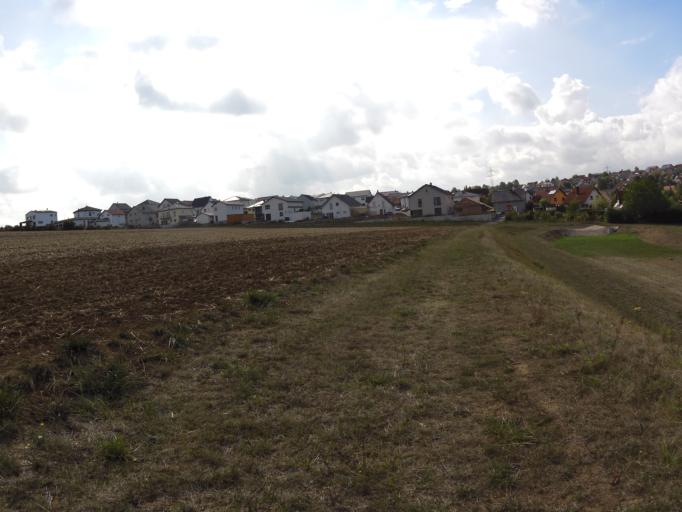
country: DE
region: Bavaria
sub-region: Regierungsbezirk Unterfranken
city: Waldbrunn
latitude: 49.7647
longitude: 9.8097
